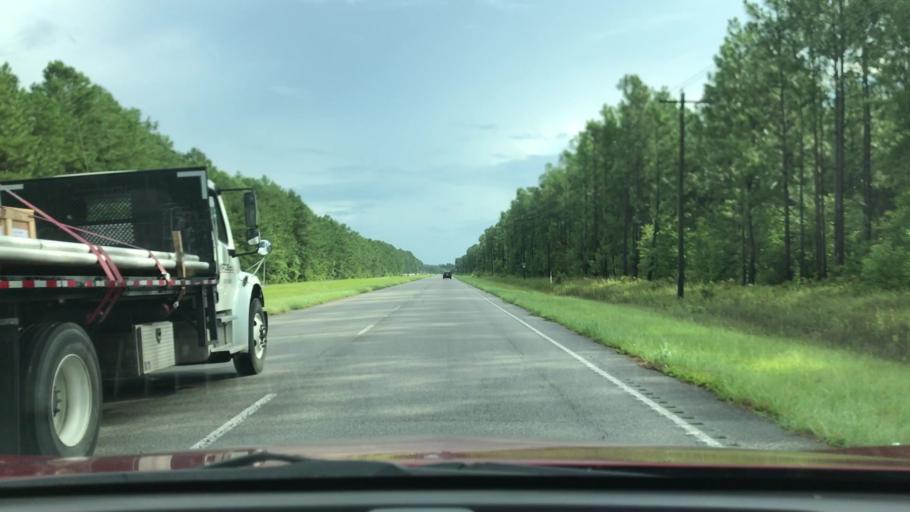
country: US
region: South Carolina
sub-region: Charleston County
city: Awendaw
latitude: 33.0157
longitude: -79.6351
